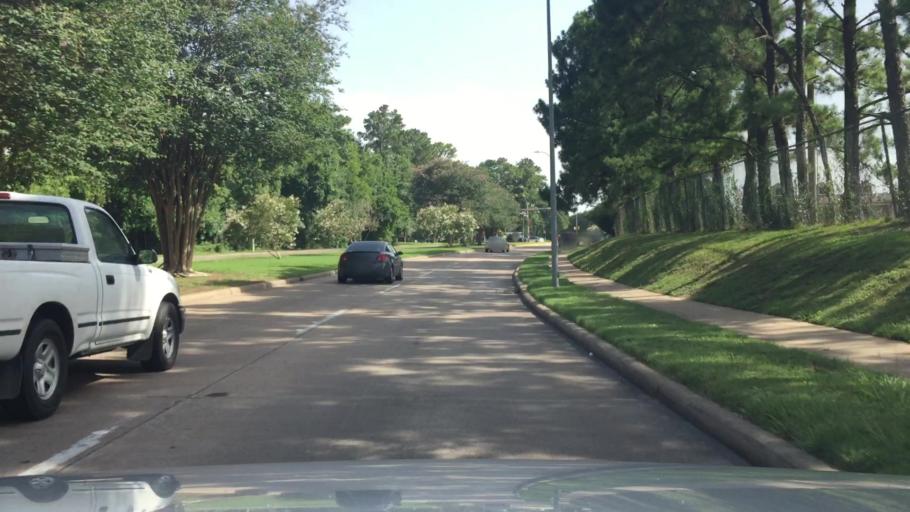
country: US
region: Texas
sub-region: Harris County
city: Bunker Hill Village
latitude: 29.7631
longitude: -95.5757
